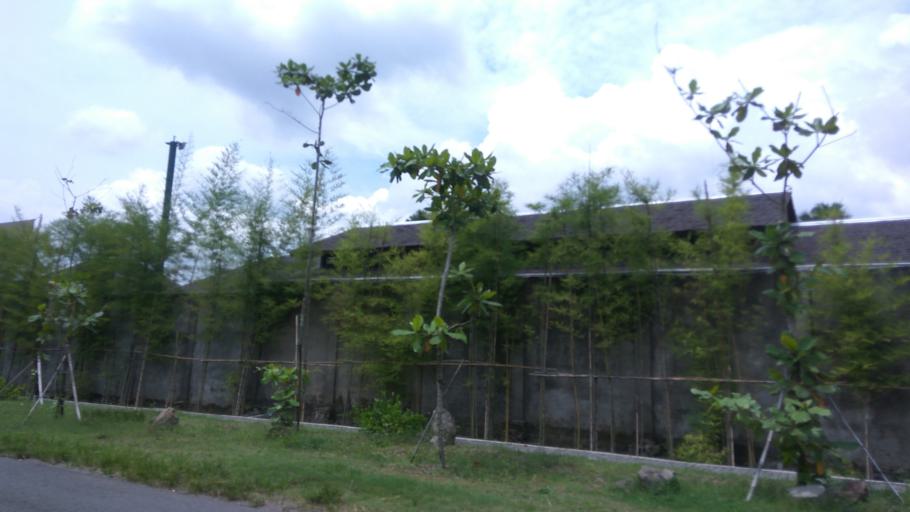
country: ID
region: Daerah Istimewa Yogyakarta
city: Depok
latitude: -7.7478
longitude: 110.4196
